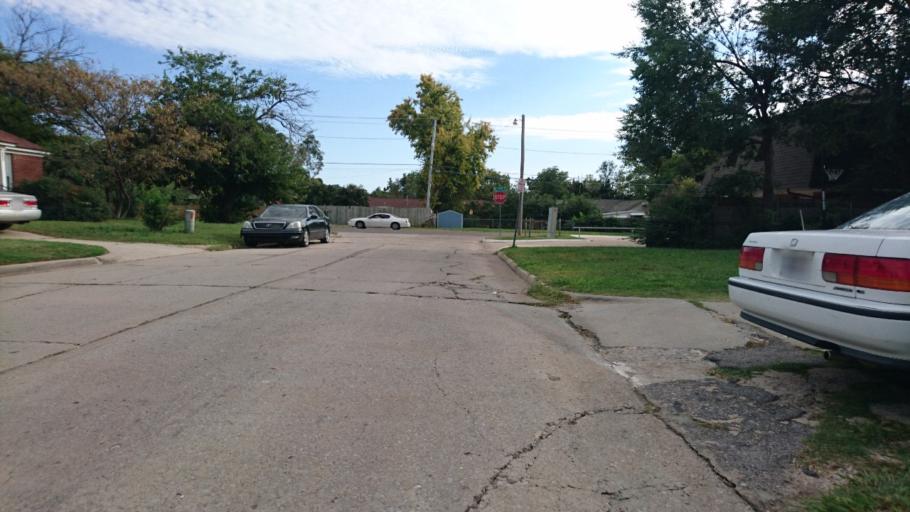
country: US
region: Oklahoma
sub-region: Oklahoma County
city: Nichols Hills
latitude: 35.5080
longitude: -97.5617
